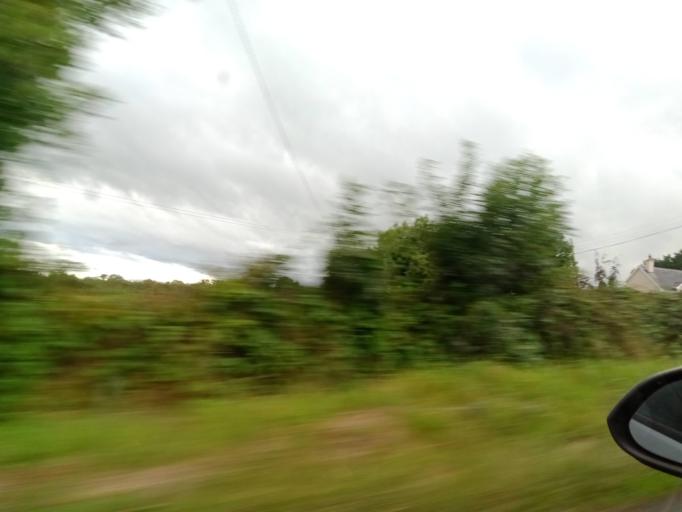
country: IE
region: Leinster
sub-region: Laois
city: Mountmellick
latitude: 53.1249
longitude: -7.3816
